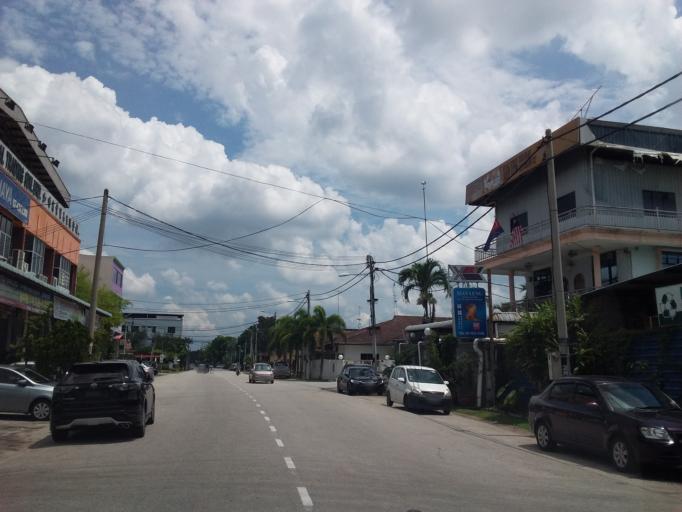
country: MY
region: Johor
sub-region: Daerah Batu Pahat
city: Batu Pahat
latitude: 1.8553
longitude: 102.9287
